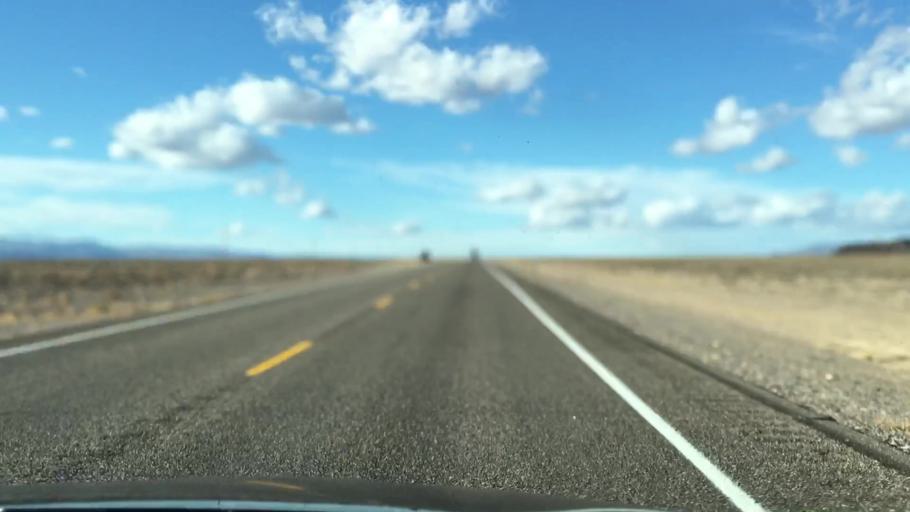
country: US
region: Nevada
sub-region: Nye County
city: Beatty
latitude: 37.1939
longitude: -116.9470
